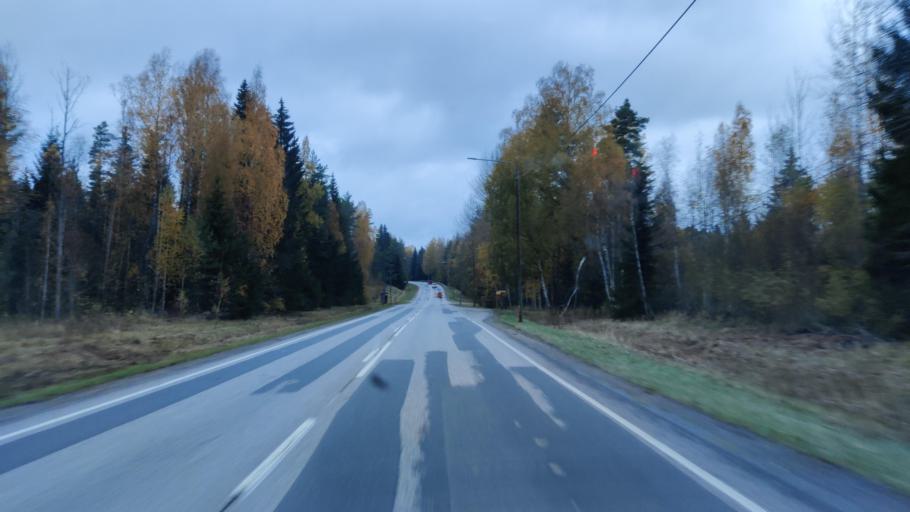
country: FI
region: Uusimaa
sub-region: Helsinki
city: Vihti
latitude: 60.3307
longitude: 24.2104
